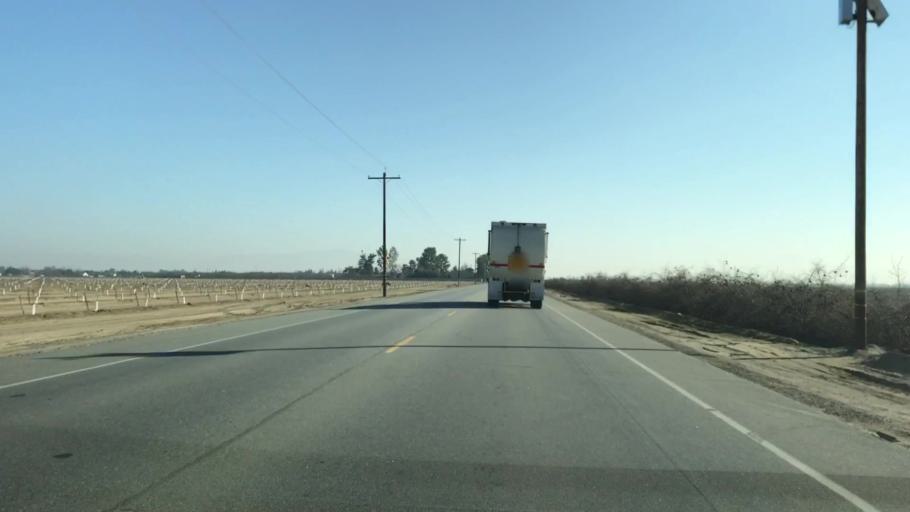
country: US
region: California
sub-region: Kern County
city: Rosedale
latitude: 35.3543
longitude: -119.2223
